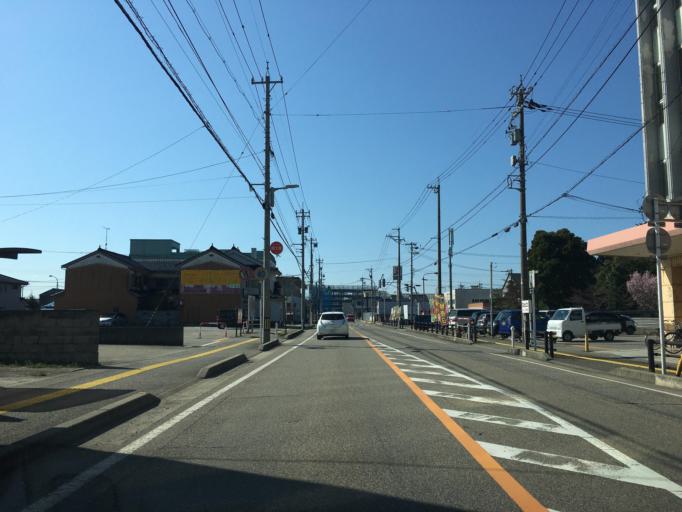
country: JP
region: Toyama
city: Nishishinminato
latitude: 36.7809
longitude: 137.0824
